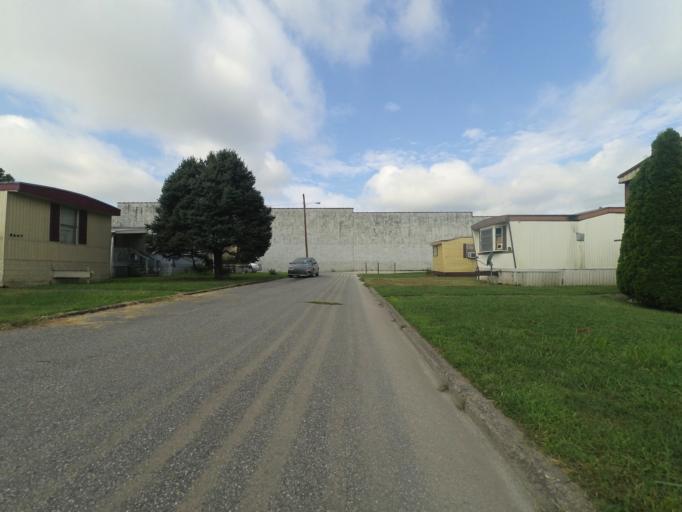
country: US
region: West Virginia
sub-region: Cabell County
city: Huntington
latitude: 38.4333
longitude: -82.4086
